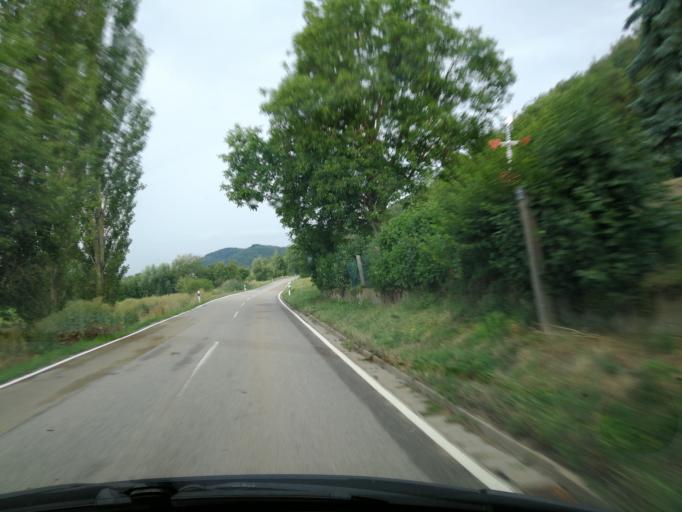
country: DE
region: Bavaria
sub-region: Upper Palatinate
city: Wiesent
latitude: 49.0176
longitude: 12.3255
